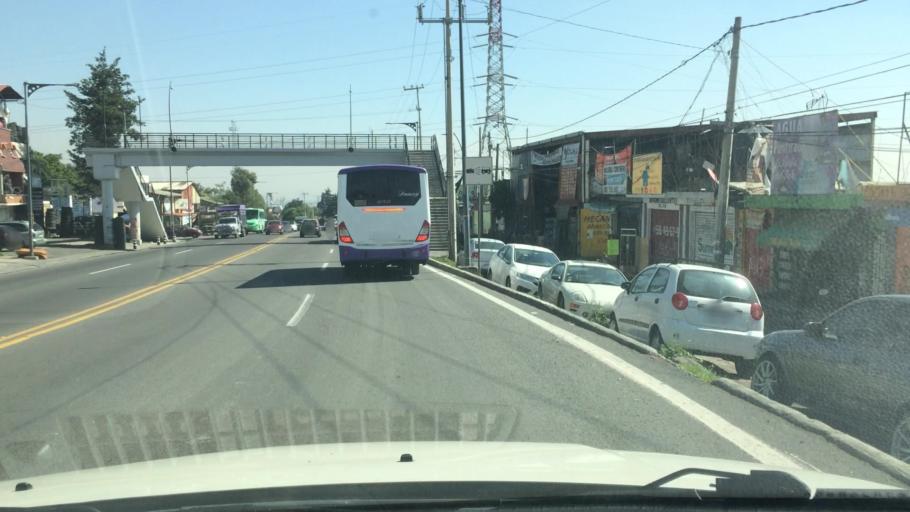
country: MX
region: Mexico City
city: Tlalpan
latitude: 19.2583
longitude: -99.1736
